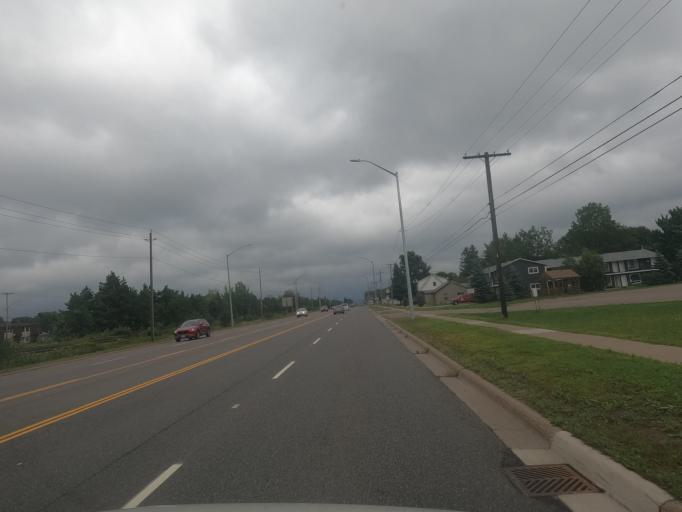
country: CA
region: Ontario
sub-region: Algoma
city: Sault Ste. Marie
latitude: 46.5253
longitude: -84.2657
